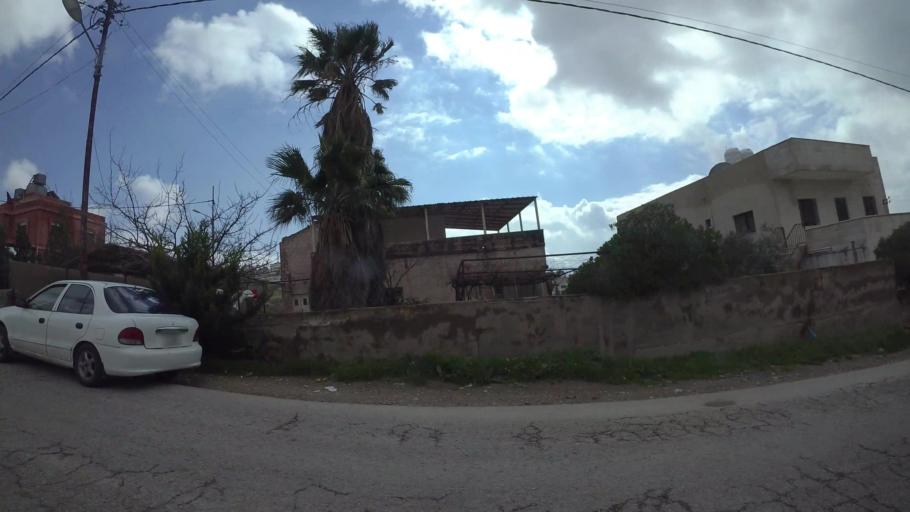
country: JO
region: Amman
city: Al Jubayhah
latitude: 32.0751
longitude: 35.8673
